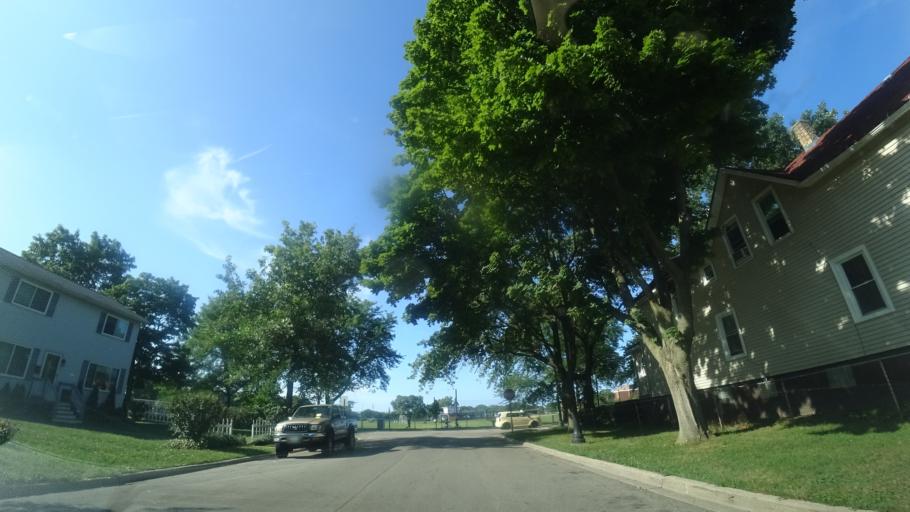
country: US
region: Illinois
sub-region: Cook County
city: Evanston
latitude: 42.0437
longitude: -87.7038
